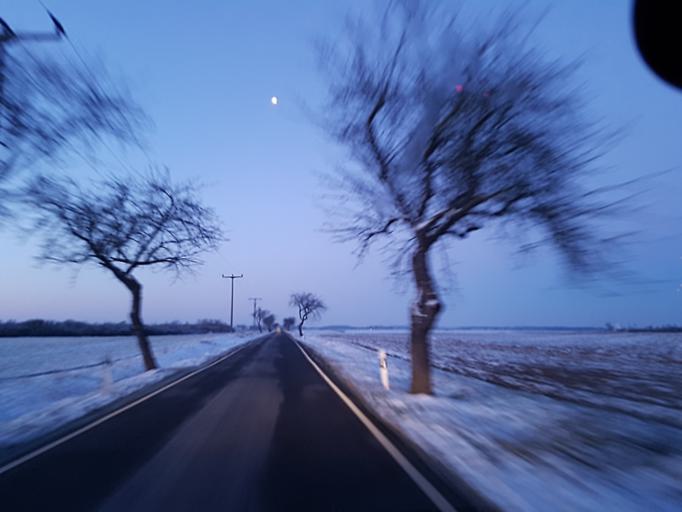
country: DE
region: Brandenburg
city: Muhlberg
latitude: 51.4685
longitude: 13.2653
